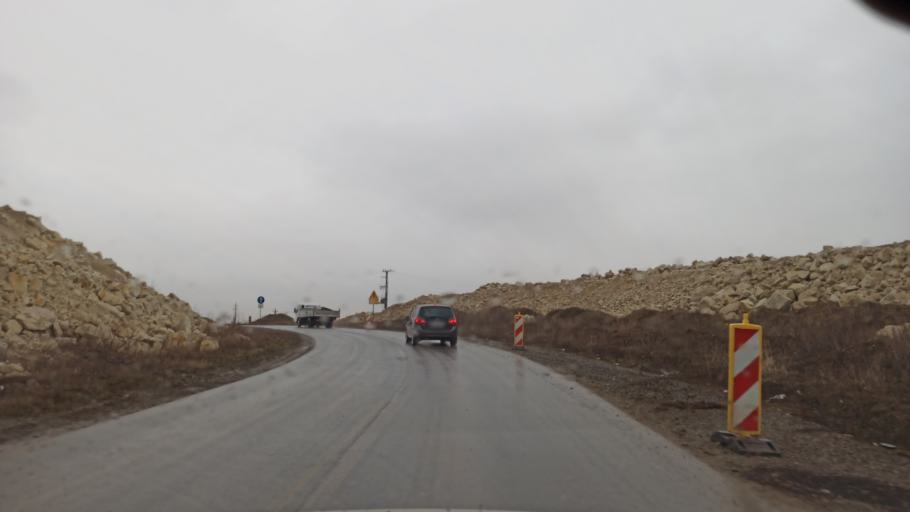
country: PL
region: Lublin Voivodeship
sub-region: Powiat lubelski
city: Niedrzwica Duza
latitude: 51.1013
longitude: 22.4076
